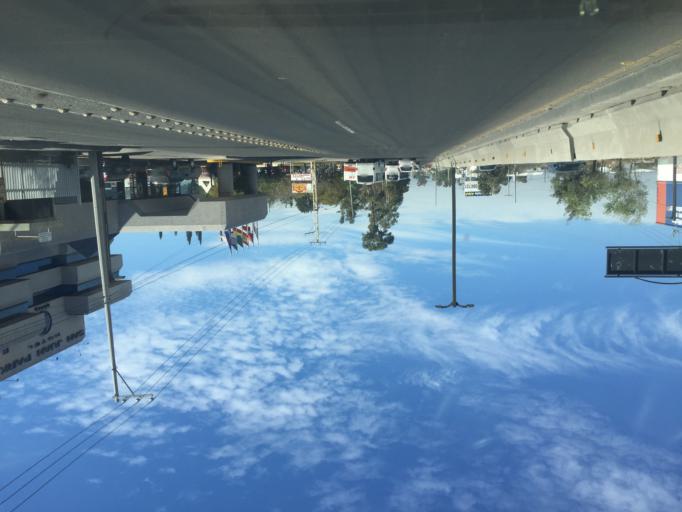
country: MX
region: Queretaro
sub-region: San Juan del Rio
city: Santa Cruz Escandon
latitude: 20.4197
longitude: -99.9794
